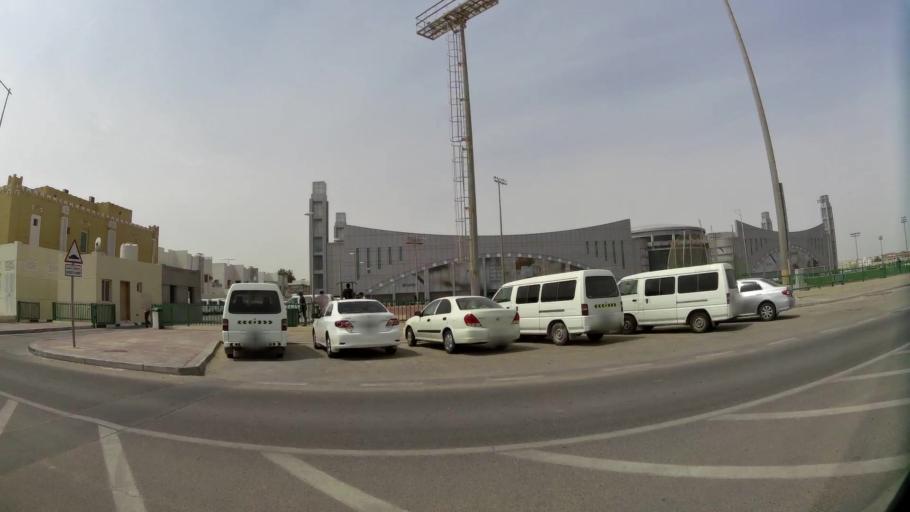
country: QA
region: Baladiyat ad Dawhah
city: Doha
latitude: 25.2660
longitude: 51.4825
